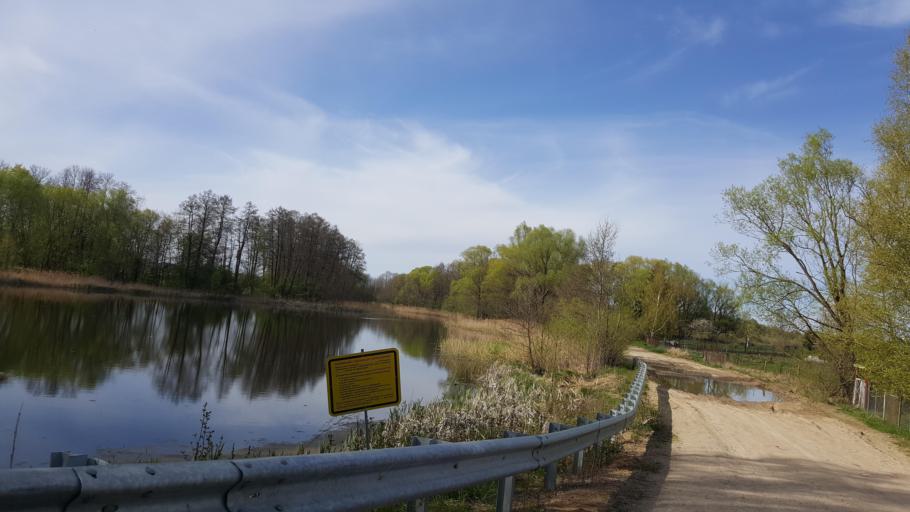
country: BY
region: Brest
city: Vysokaye
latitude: 52.3913
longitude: 23.4145
